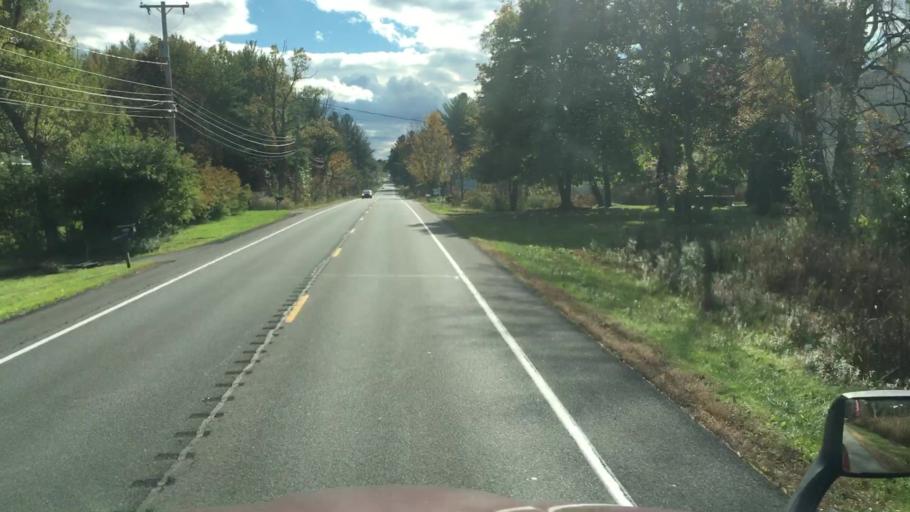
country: US
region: New York
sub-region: Saratoga County
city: Ballston Spa
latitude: 42.9476
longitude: -73.8685
